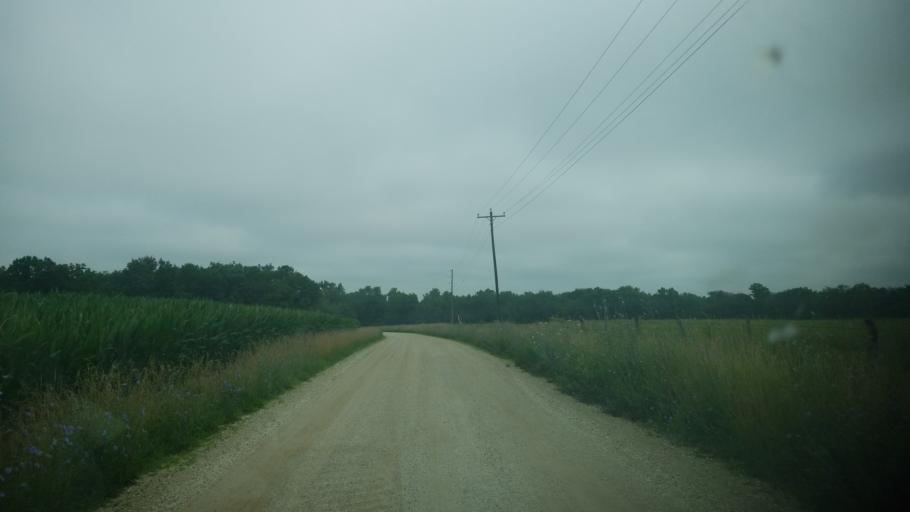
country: US
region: Missouri
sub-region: Pike County
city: Bowling Green
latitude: 39.3541
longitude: -91.2617
